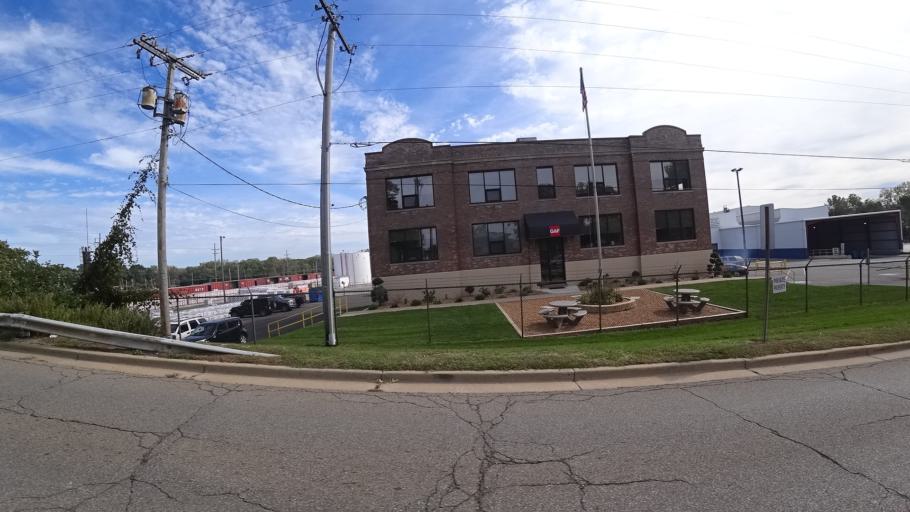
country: US
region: Indiana
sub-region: LaPorte County
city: Trail Creek
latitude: 41.7125
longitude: -86.8649
